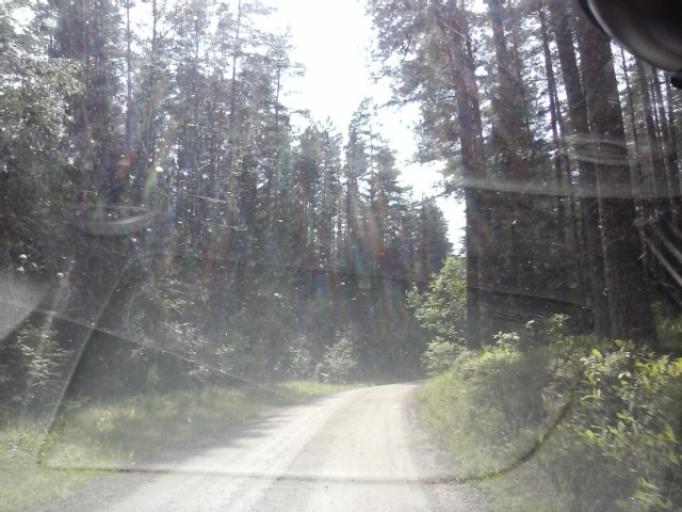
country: EE
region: Tartu
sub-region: UElenurme vald
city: Ulenurme
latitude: 58.2591
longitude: 26.9407
